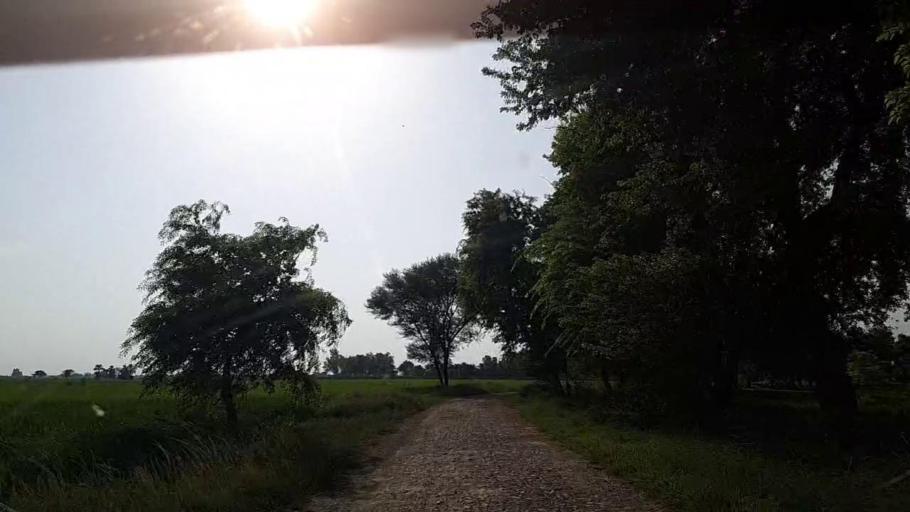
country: PK
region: Sindh
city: Khanpur
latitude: 27.8424
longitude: 69.3728
